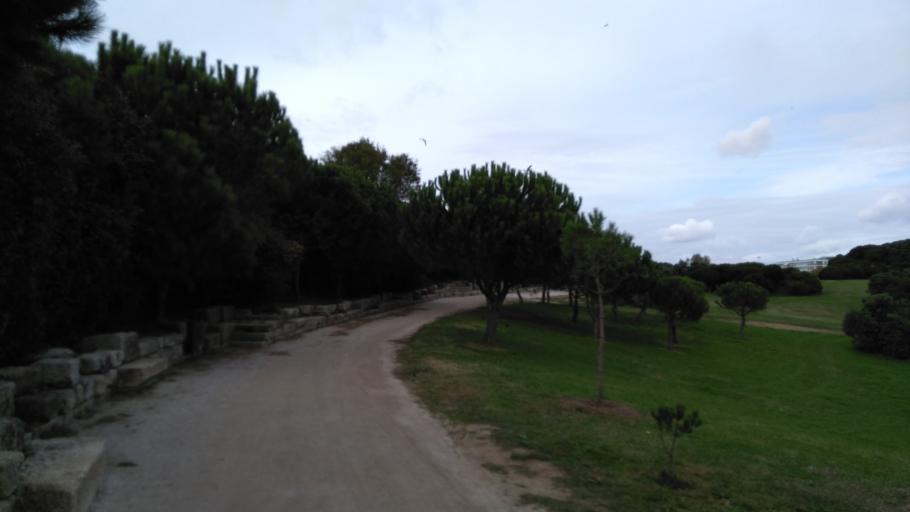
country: PT
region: Porto
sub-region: Matosinhos
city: Matosinhos
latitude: 41.1688
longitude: -8.6850
